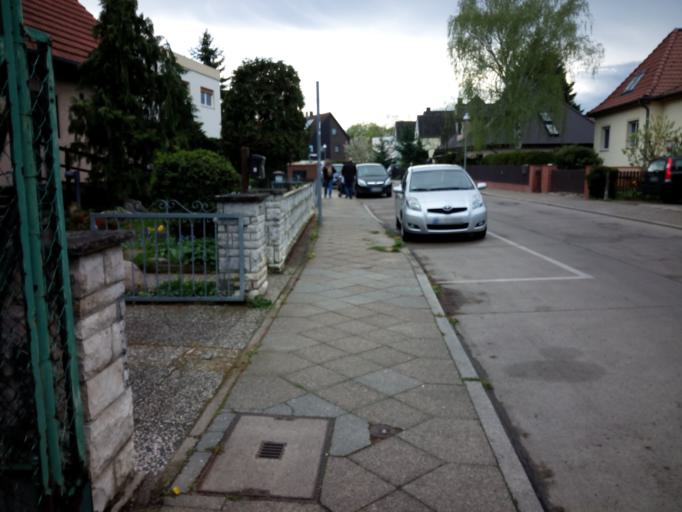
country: DE
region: Berlin
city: Rudow
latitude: 52.4265
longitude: 13.4974
